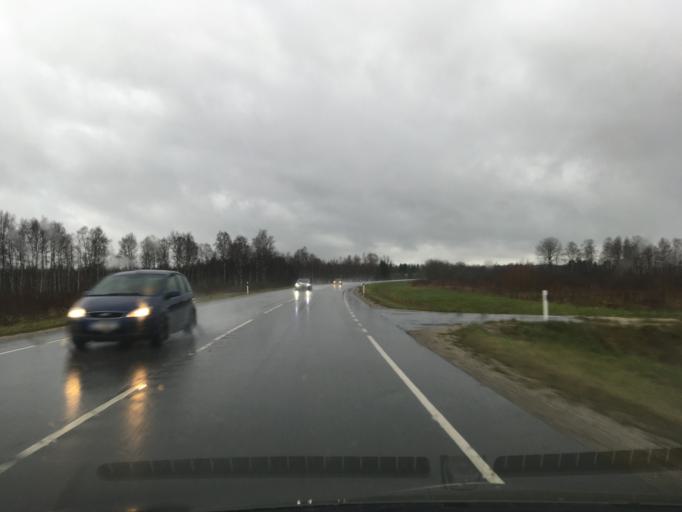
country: EE
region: Laeaene
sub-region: Lihula vald
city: Lihula
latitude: 58.7960
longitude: 24.0445
